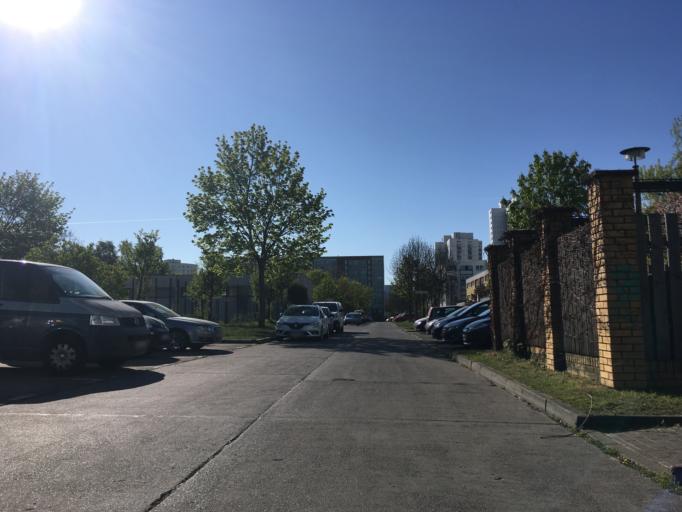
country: DE
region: Berlin
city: Neu-Hohenschoenhausen
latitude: 52.5708
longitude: 13.5124
